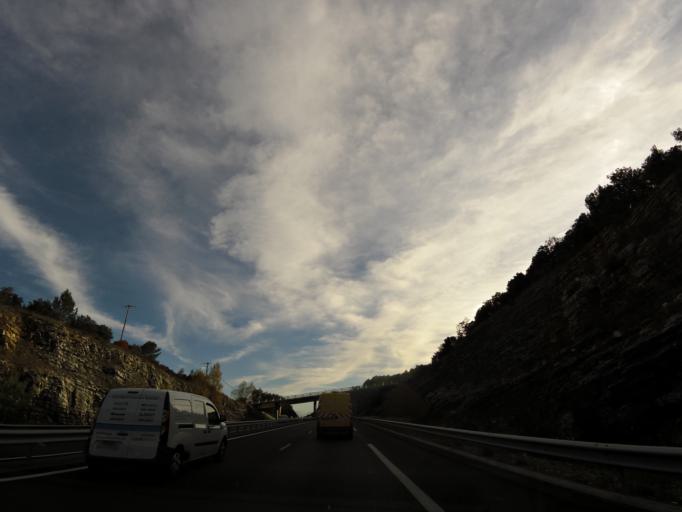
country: FR
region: Languedoc-Roussillon
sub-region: Departement du Gard
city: Vezenobres
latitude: 44.0545
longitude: 4.1230
